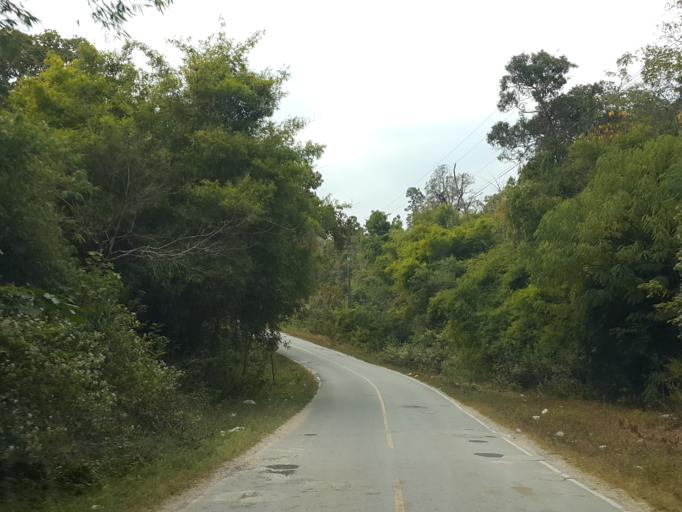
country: TH
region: Chiang Mai
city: Om Koi
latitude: 17.7986
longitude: 98.3440
